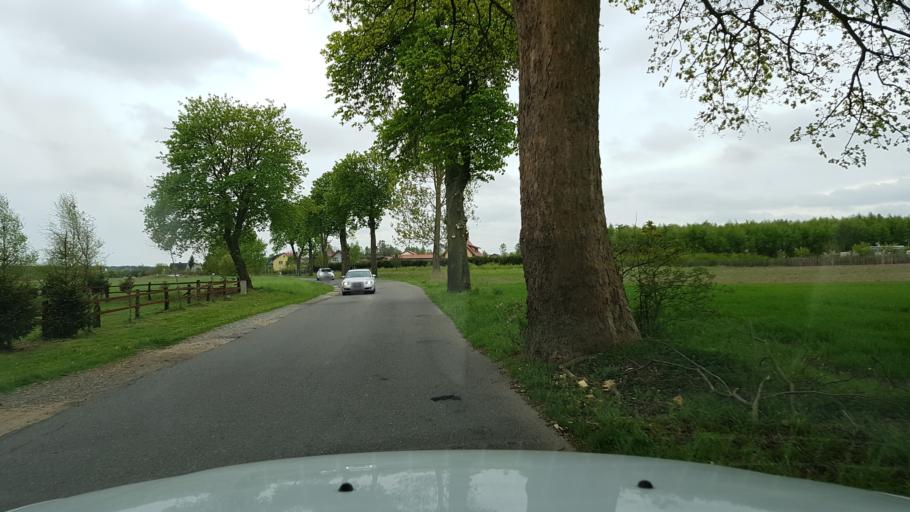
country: PL
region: West Pomeranian Voivodeship
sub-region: Powiat slawienski
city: Slawno
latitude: 54.4040
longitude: 16.7179
